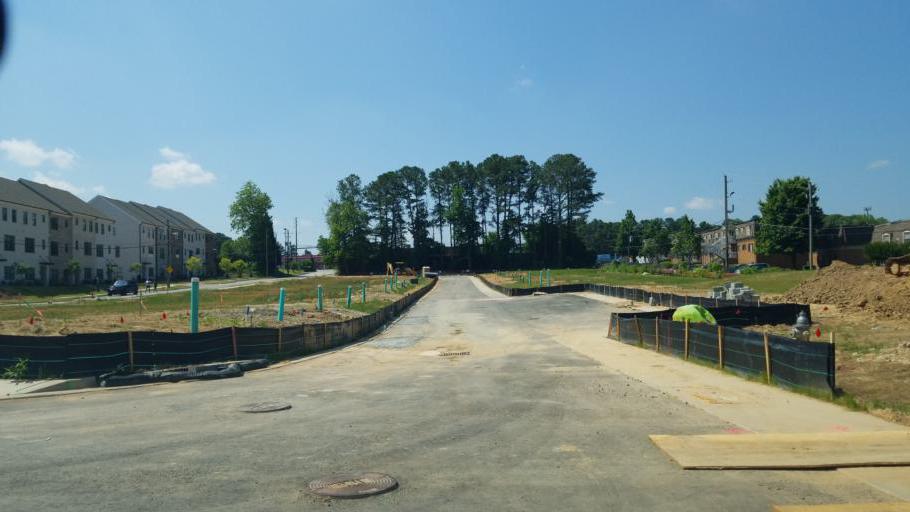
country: US
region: Georgia
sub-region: Cobb County
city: Vinings
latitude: 33.8854
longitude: -84.4805
